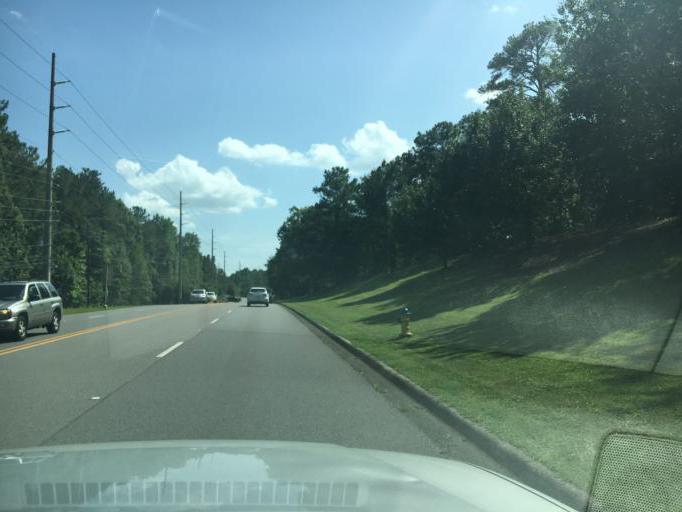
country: US
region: Alabama
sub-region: Shelby County
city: Meadowbrook
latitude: 33.4088
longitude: -86.7034
